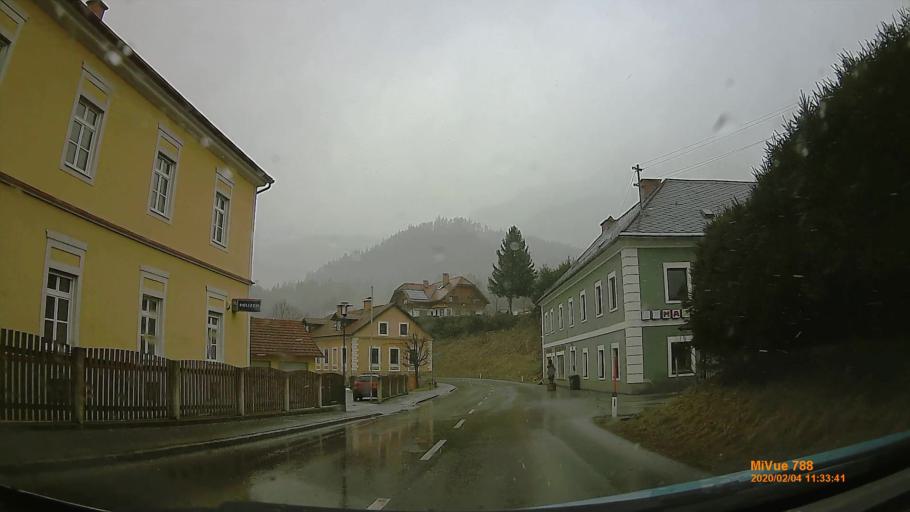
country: AT
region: Styria
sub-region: Politischer Bezirk Bruck-Muerzzuschlag
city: Neuberg an der Muerz
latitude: 47.6654
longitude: 15.5757
